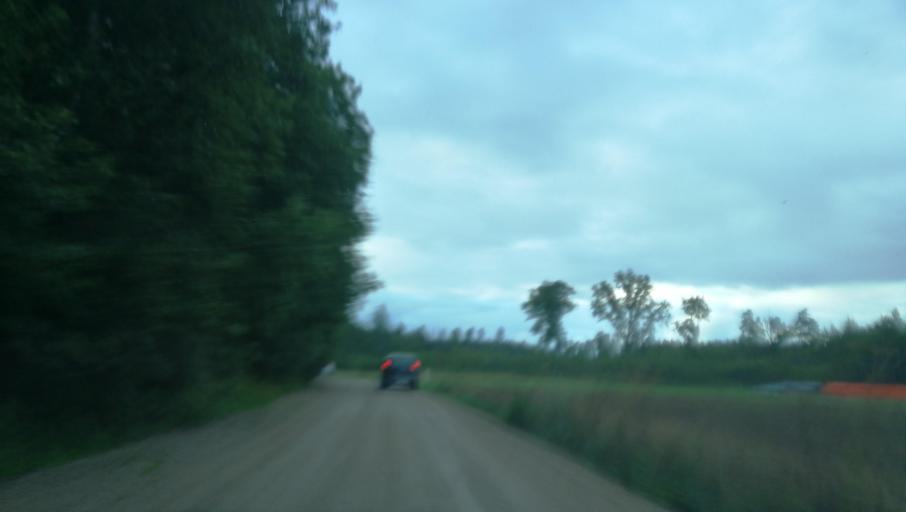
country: LV
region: Incukalns
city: Incukalns
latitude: 57.0286
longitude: 24.7939
